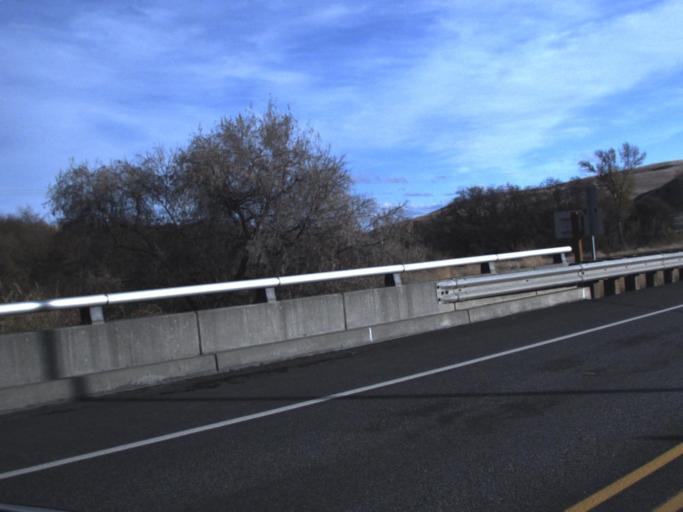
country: US
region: Washington
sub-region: Columbia County
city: Dayton
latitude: 46.4887
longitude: -117.9615
